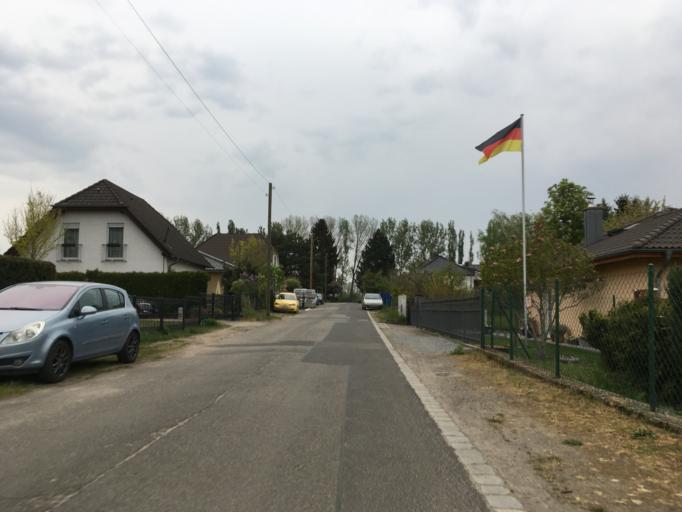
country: DE
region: Berlin
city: Stadtrandsiedlung Malchow
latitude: 52.5845
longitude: 13.4964
